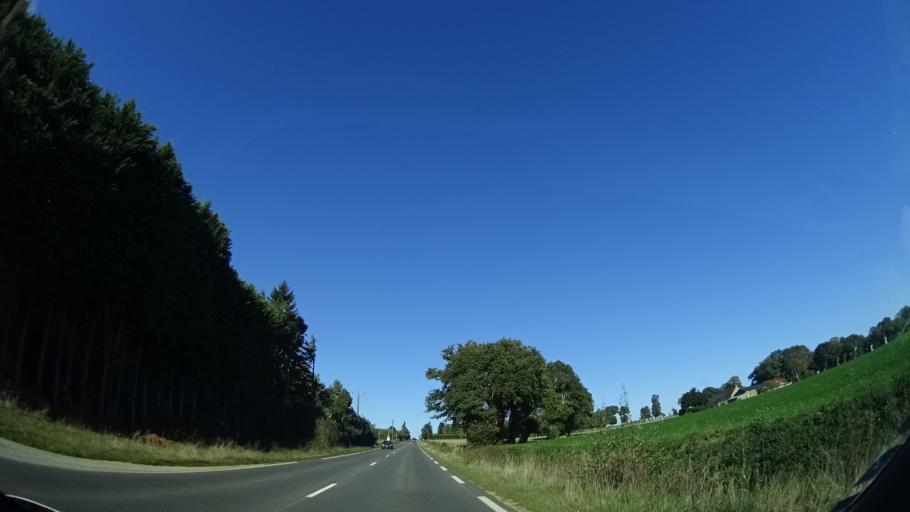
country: FR
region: Brittany
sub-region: Departement d'Ille-et-Vilaine
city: Melesse
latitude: 48.1892
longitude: -1.6931
